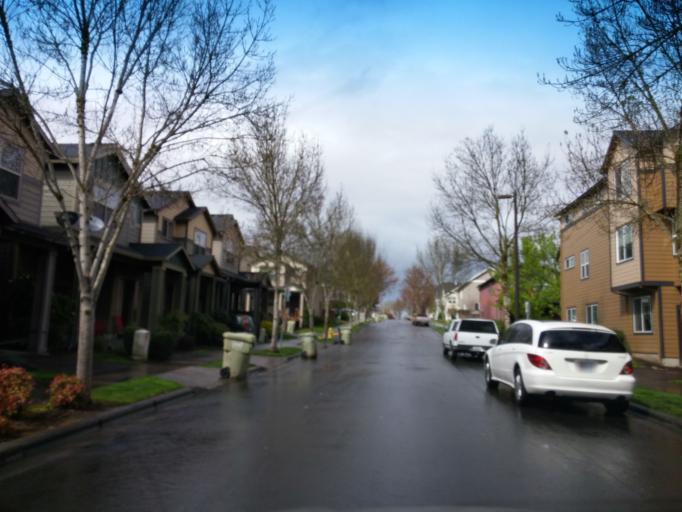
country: US
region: Oregon
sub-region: Washington County
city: Aloha
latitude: 45.5087
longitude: -122.8573
